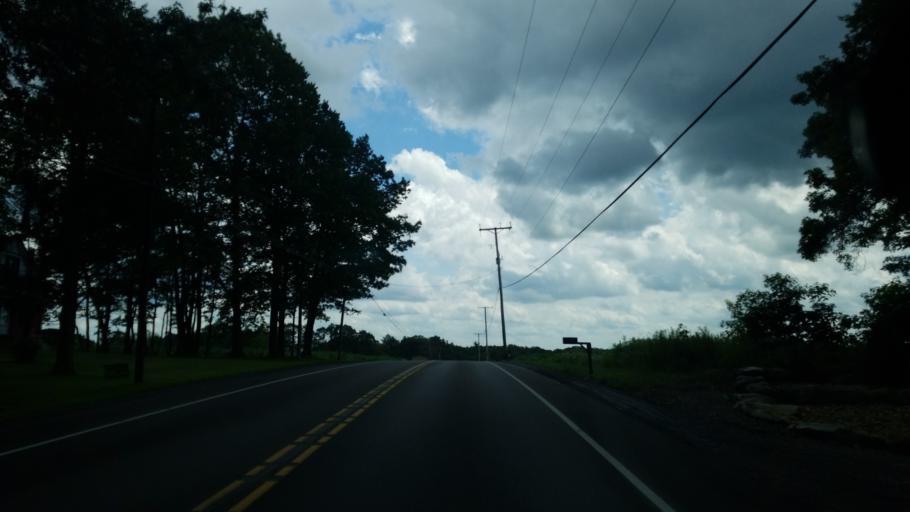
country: US
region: Pennsylvania
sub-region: Jefferson County
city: Brookville
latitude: 41.2636
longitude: -79.1079
